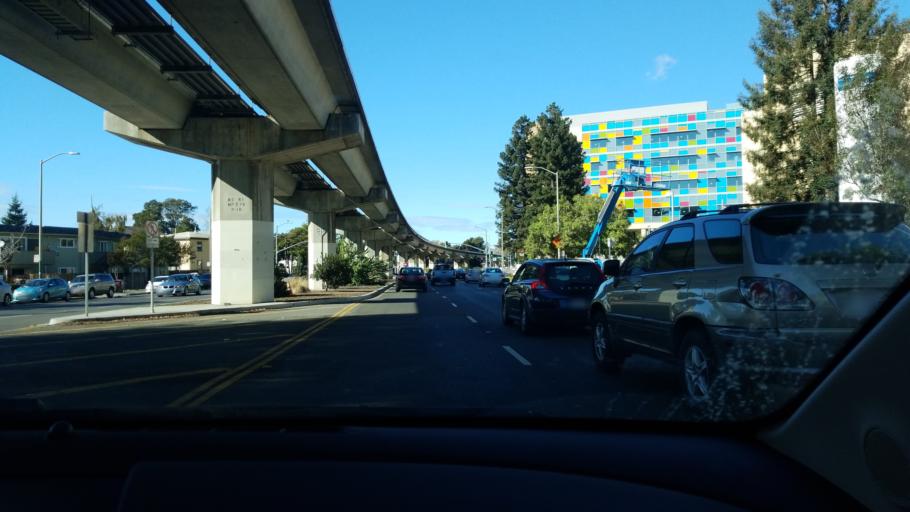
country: US
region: California
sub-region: Alameda County
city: Emeryville
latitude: 37.8363
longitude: -122.2677
